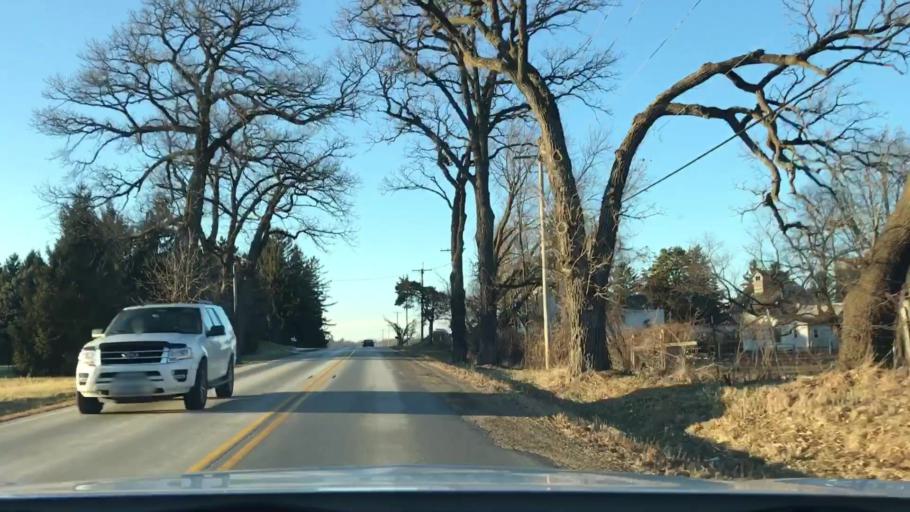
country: US
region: Illinois
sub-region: Kane County
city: Gilberts
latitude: 42.0825
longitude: -88.3848
